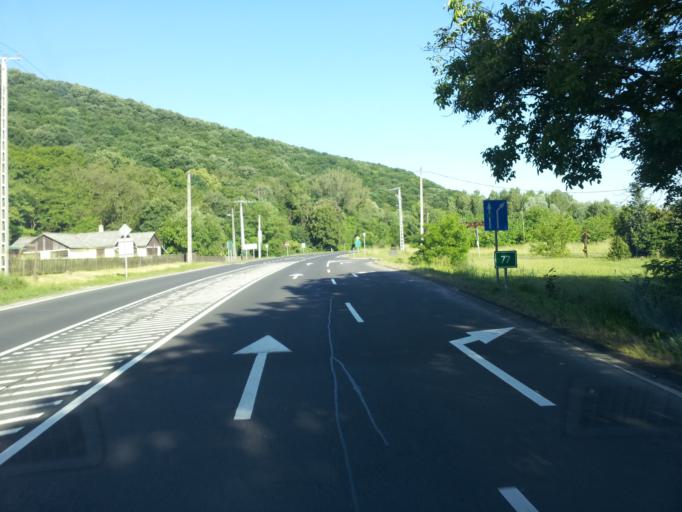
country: SK
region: Nitriansky
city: Sahy
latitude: 48.0475
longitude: 18.9827
